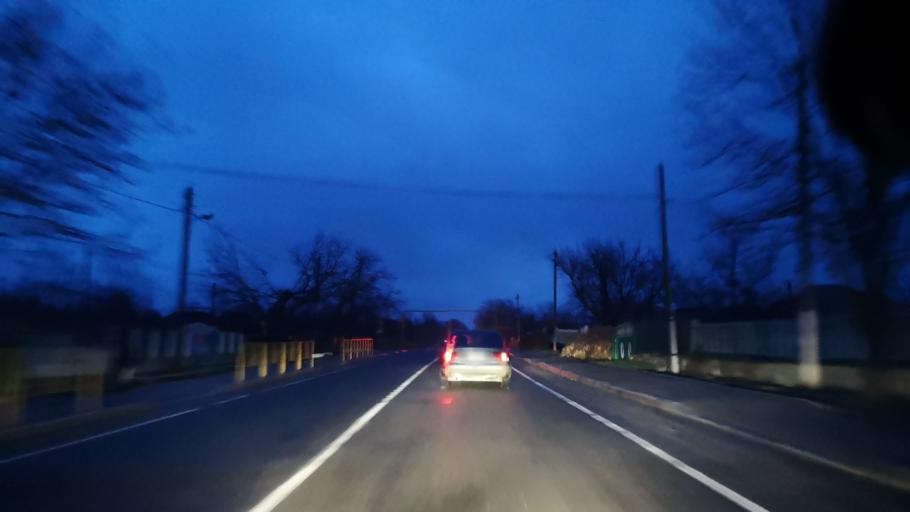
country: MD
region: Orhei
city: Orhei
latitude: 47.4351
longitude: 28.7981
